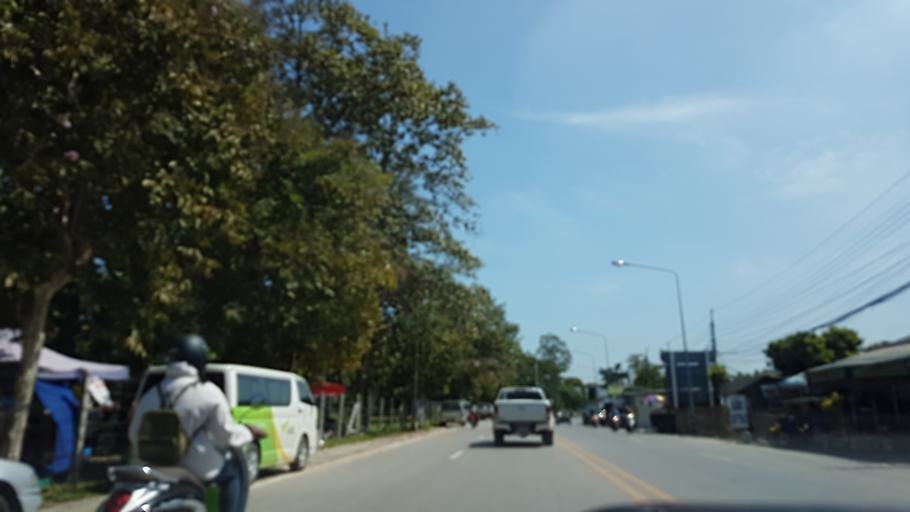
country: TH
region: Chiang Mai
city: Chiang Mai
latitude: 18.8206
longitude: 98.9711
